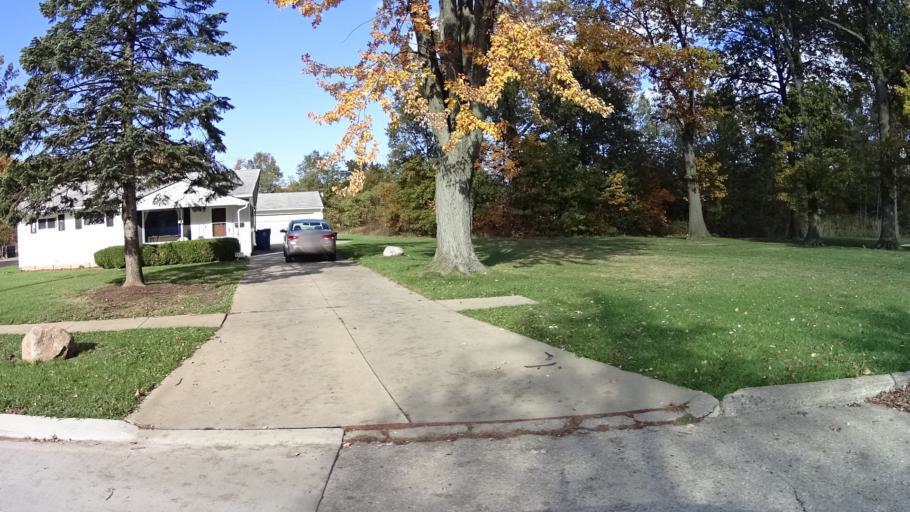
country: US
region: Ohio
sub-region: Lorain County
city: Sheffield
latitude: 41.4370
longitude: -82.1238
